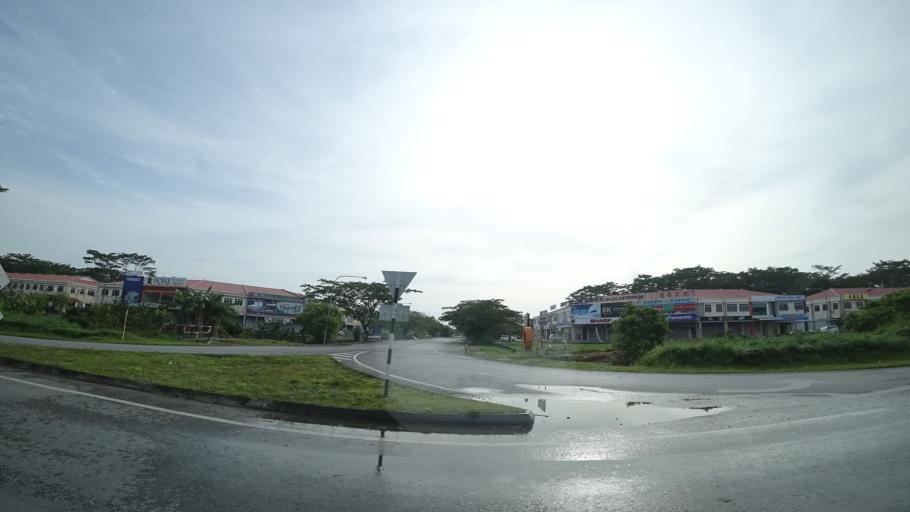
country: MY
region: Sarawak
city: Miri
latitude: 4.4747
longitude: 114.0420
